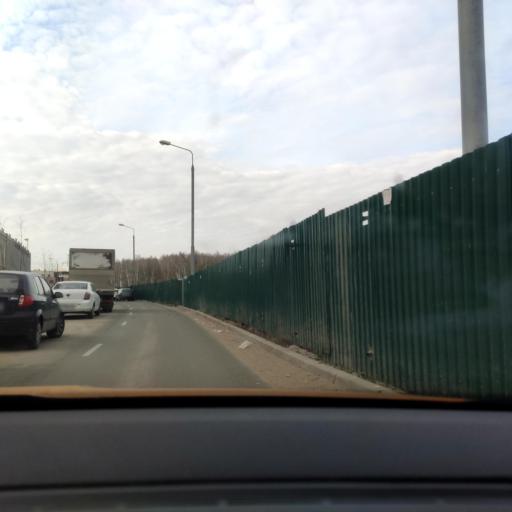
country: RU
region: Moskovskaya
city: Odintsovo
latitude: 55.6820
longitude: 37.2442
